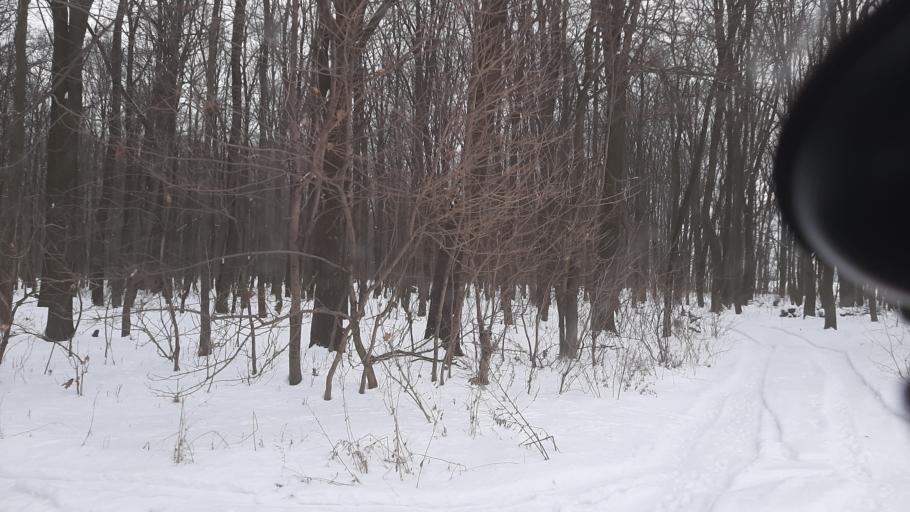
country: PL
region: Lublin Voivodeship
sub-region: Powiat lubelski
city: Garbow
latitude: 51.3688
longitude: 22.3883
